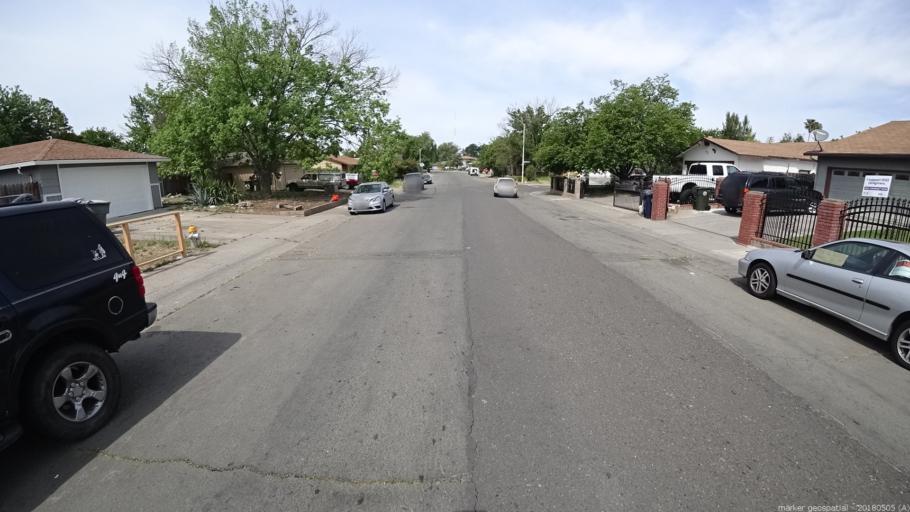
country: US
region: California
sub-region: Sacramento County
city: Rio Linda
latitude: 38.6478
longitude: -121.4652
